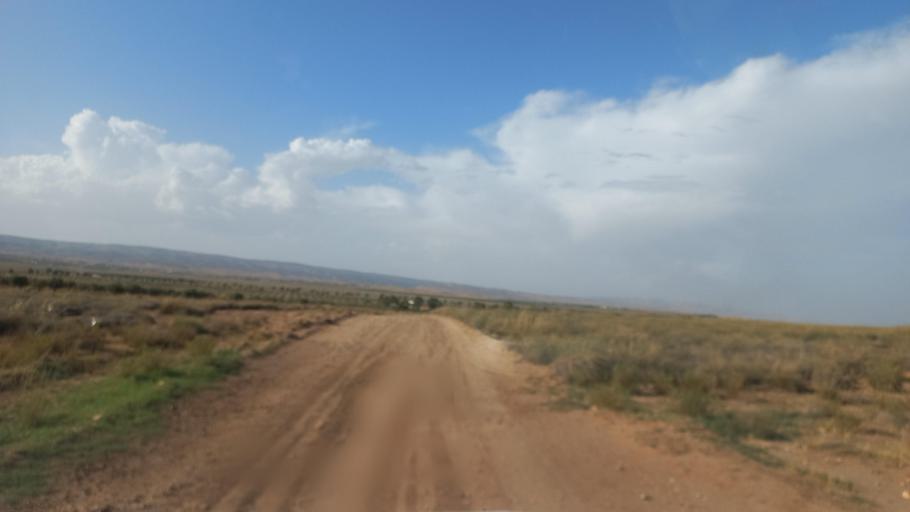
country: TN
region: Al Qasrayn
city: Kasserine
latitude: 35.2199
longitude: 8.9698
